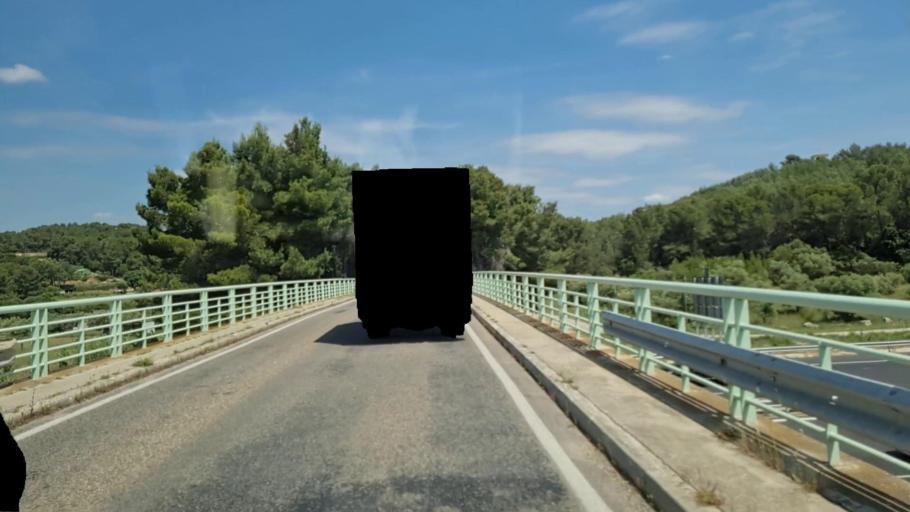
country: FR
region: Languedoc-Roussillon
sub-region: Departement du Gard
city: Saint-Gervasy
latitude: 43.8803
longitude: 4.4683
